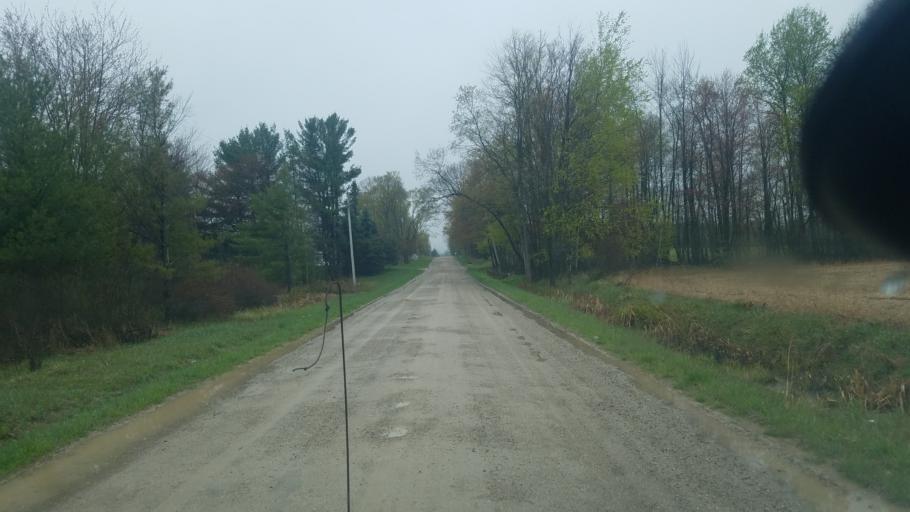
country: US
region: Michigan
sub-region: Montcalm County
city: Lakeview
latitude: 43.4886
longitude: -85.3333
